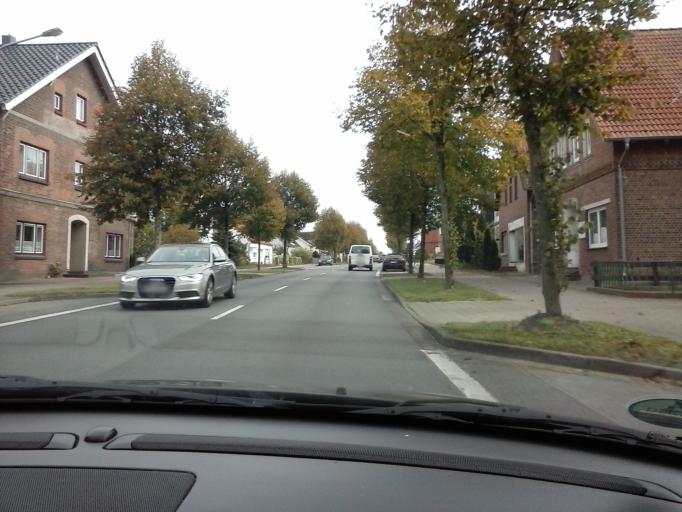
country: DE
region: Lower Saxony
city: Hemmoor
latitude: 53.7017
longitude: 9.1358
